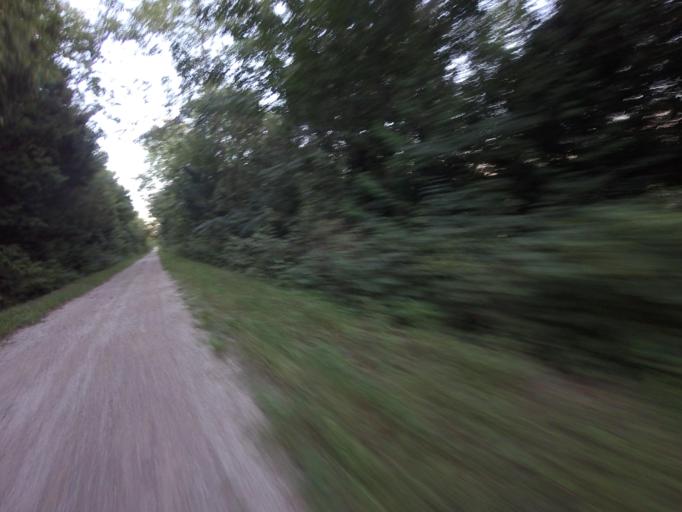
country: CA
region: Ontario
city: Goderich
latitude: 43.7527
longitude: -81.6133
